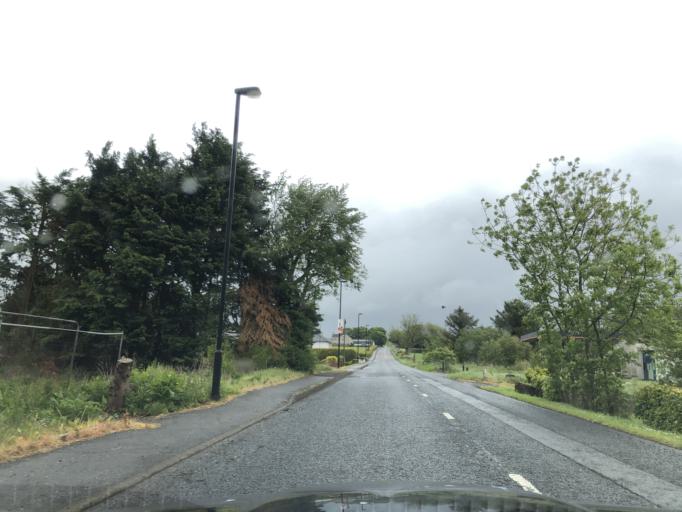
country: GB
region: Northern Ireland
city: Bushmills
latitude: 55.1554
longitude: -6.4064
